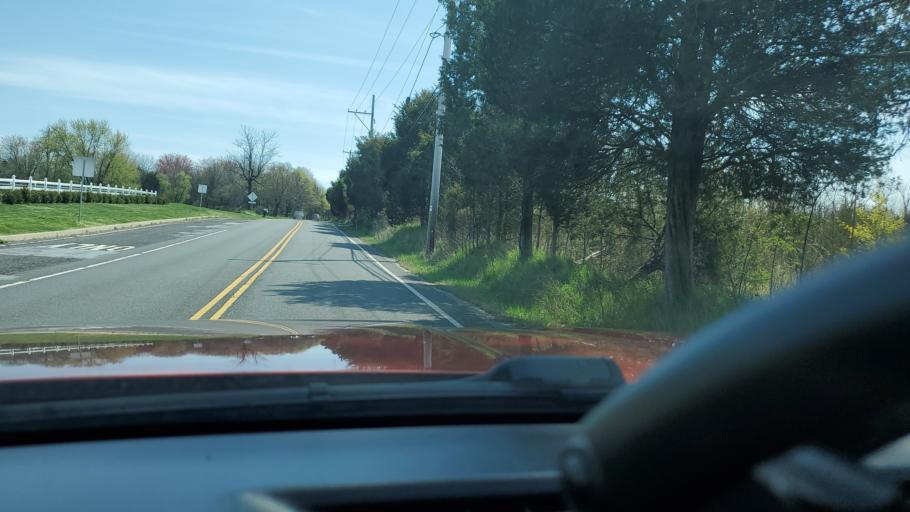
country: US
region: Pennsylvania
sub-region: Montgomery County
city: Red Hill
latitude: 40.3535
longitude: -75.4818
